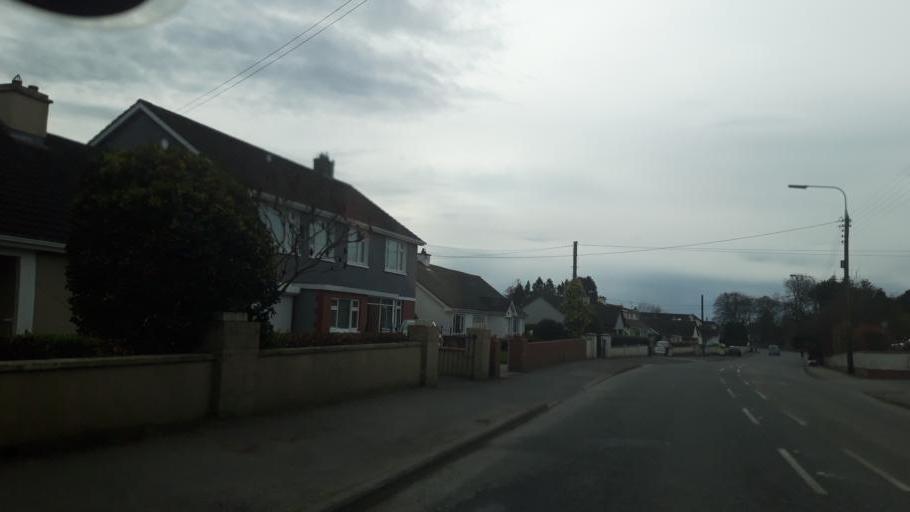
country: IE
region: Leinster
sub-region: Uibh Fhaili
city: Edenderry
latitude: 53.3346
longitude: -7.0648
